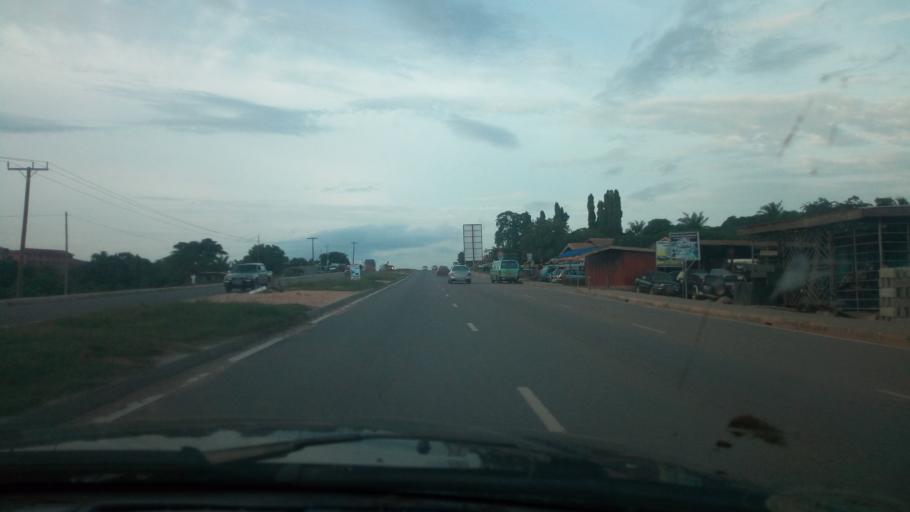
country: GH
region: Western
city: Takoradi
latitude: 4.9191
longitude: -1.7887
